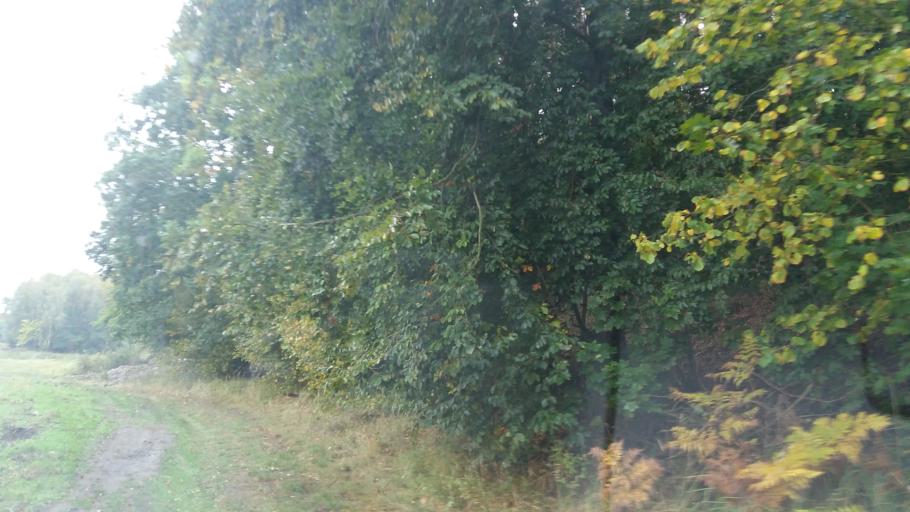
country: PL
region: West Pomeranian Voivodeship
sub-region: Powiat choszczenski
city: Pelczyce
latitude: 53.0708
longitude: 15.2818
